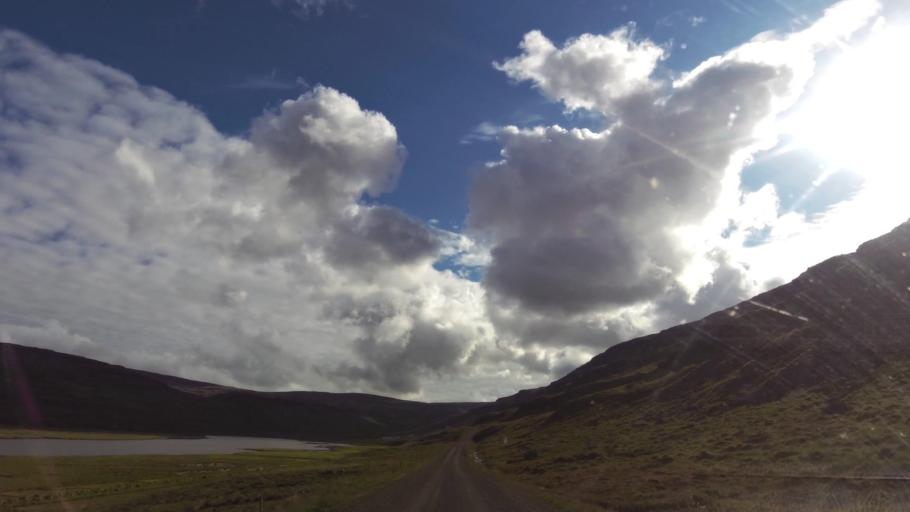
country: IS
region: West
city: Olafsvik
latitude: 65.5723
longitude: -24.1607
